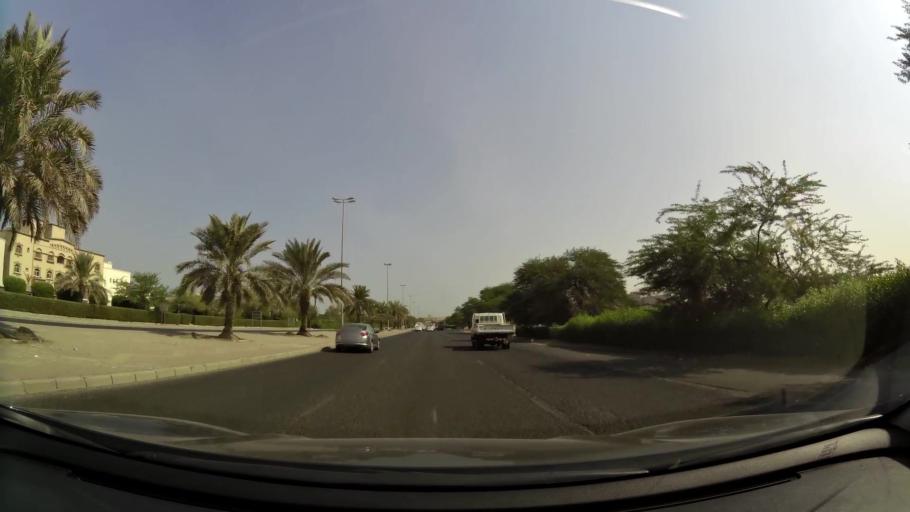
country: KW
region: Al Ahmadi
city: Al Fahahil
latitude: 29.0917
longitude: 48.1088
